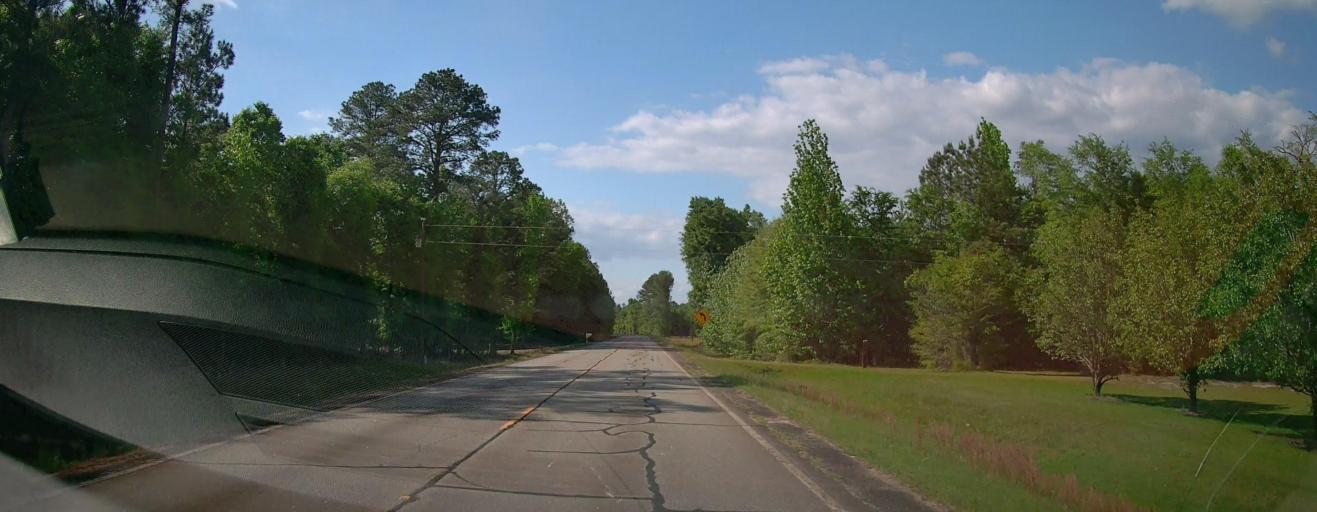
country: US
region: Georgia
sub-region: Washington County
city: Tennille
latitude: 32.9021
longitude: -82.9697
